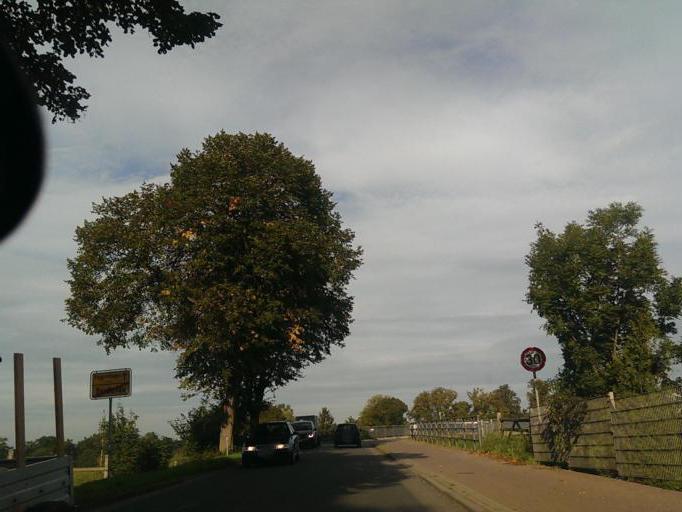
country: DE
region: Lower Saxony
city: Neustadt am Rubenberge
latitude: 52.4620
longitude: 9.4751
